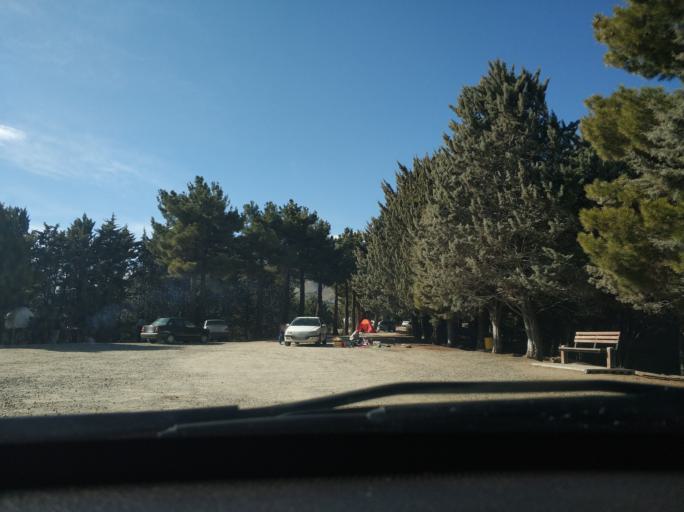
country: IR
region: Tehran
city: Tajrish
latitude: 35.8020
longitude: 51.5670
